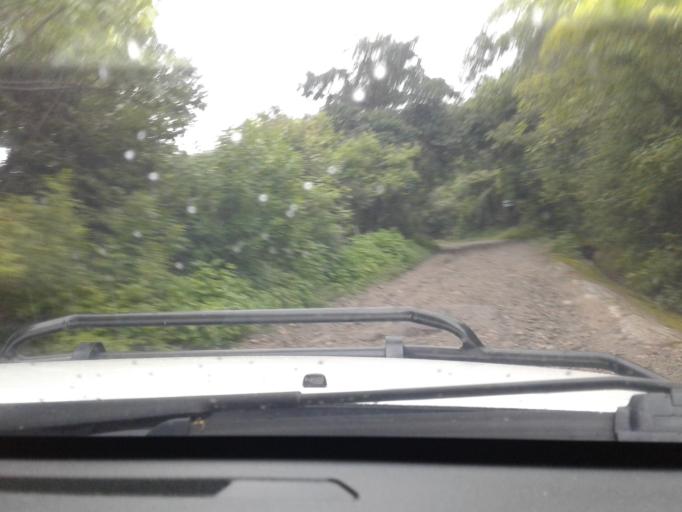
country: NI
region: Leon
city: Santa Rosa del Penon
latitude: 12.9016
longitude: -86.2307
